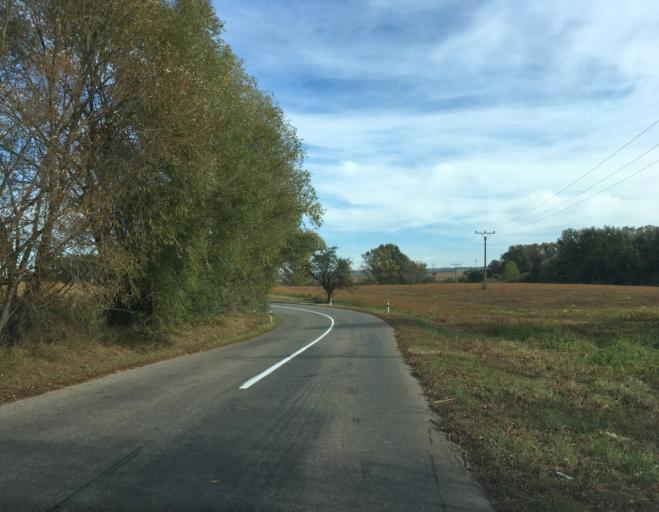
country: SK
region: Nitriansky
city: Svodin
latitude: 48.0003
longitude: 18.4114
